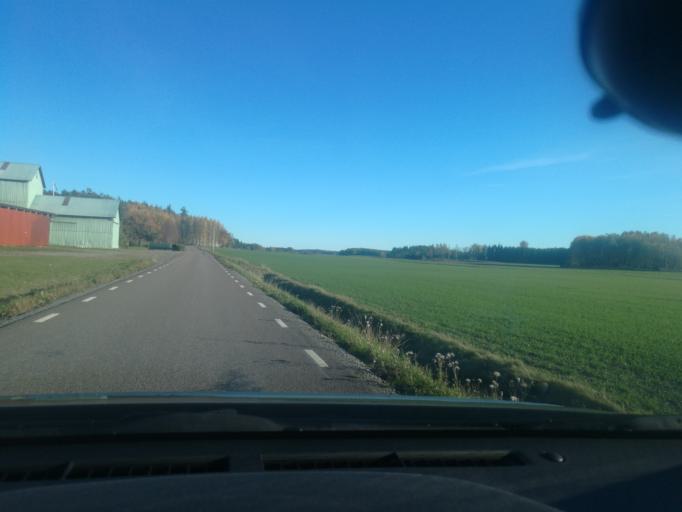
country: SE
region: Vaestmanland
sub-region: Kopings Kommun
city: Koping
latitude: 59.5782
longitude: 16.0037
